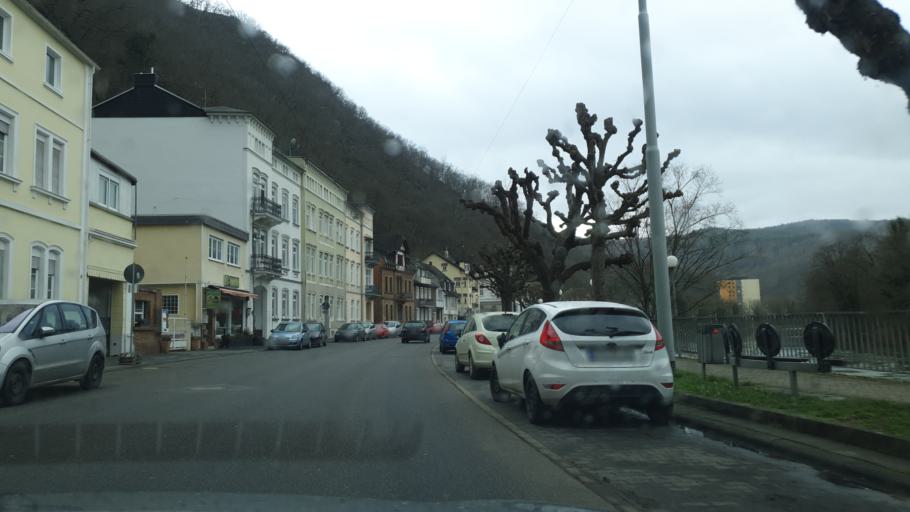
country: DE
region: Rheinland-Pfalz
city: Bad Ems
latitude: 50.3271
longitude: 7.7327
